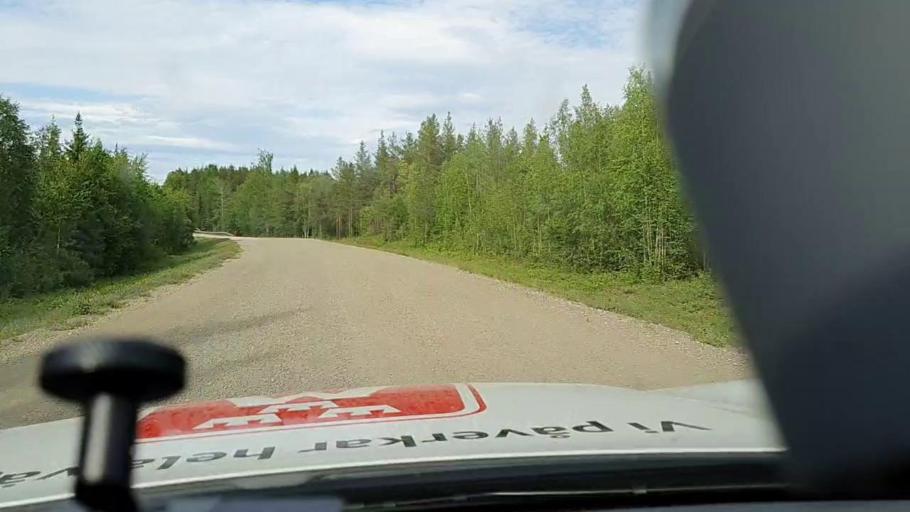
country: SE
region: Norrbotten
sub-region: Alvsbyns Kommun
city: AElvsbyn
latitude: 66.1487
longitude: 21.0290
